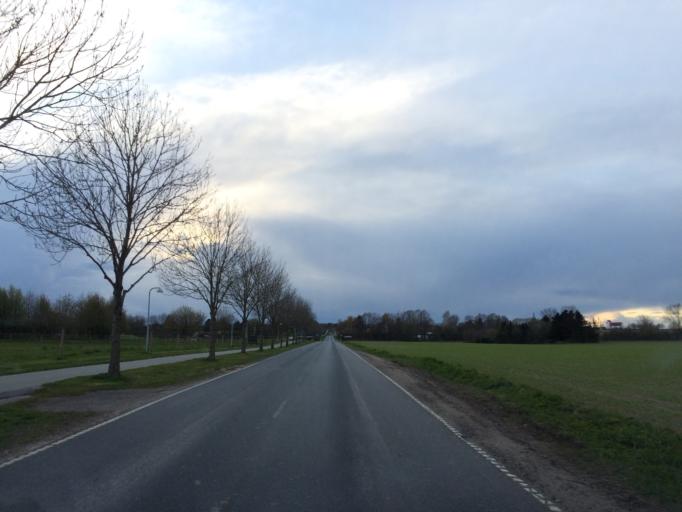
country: DK
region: South Denmark
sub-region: Odense Kommune
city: Bellinge
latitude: 55.3430
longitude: 10.2894
